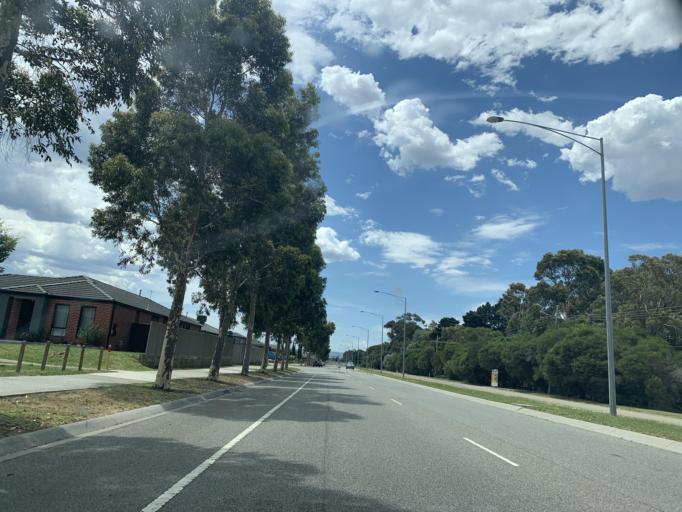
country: AU
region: Victoria
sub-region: Casey
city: Cranbourne East
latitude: -38.1144
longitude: 145.3088
